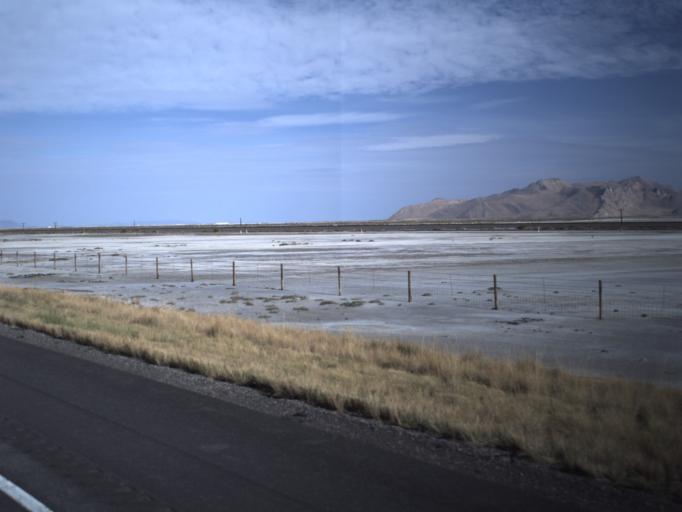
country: US
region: Utah
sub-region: Tooele County
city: Grantsville
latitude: 40.6944
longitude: -112.4707
